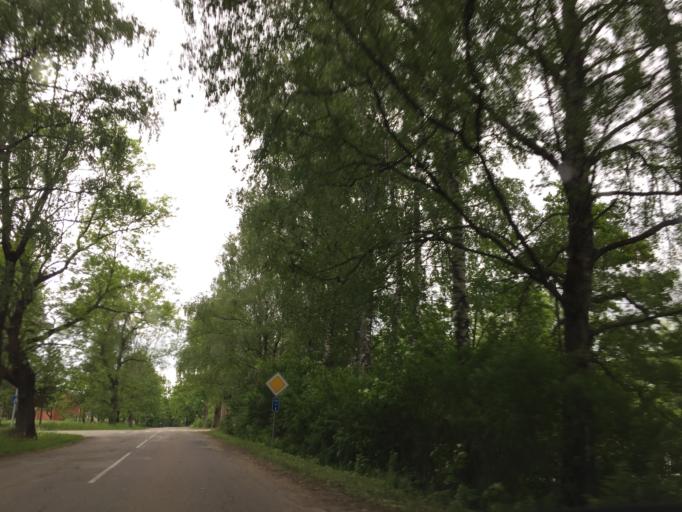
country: LV
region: Preilu Rajons
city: Preili
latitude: 56.0619
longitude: 26.7704
